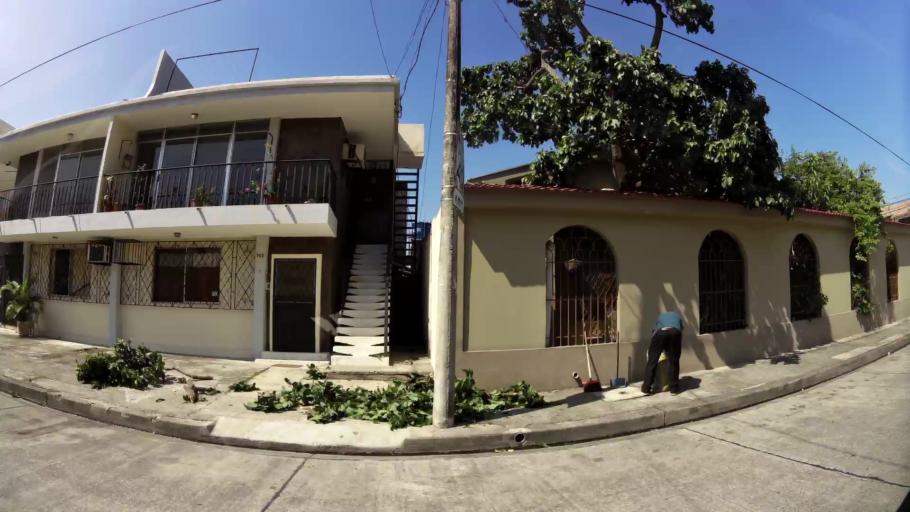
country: EC
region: Guayas
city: Guayaquil
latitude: -2.1687
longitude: -79.9135
